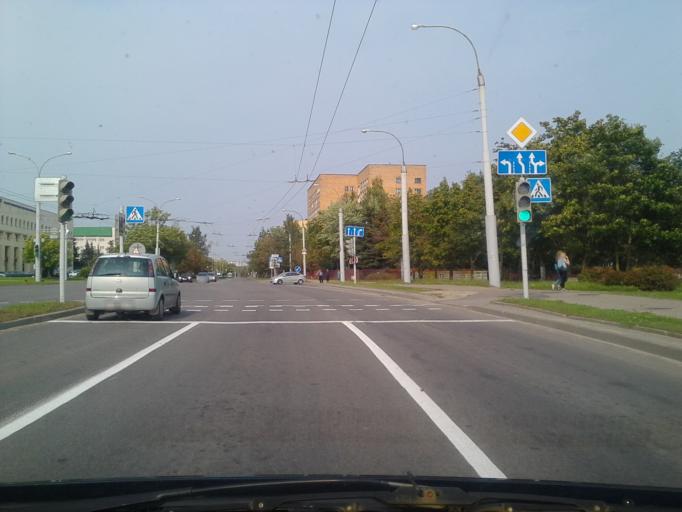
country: BY
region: Minsk
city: Syenitsa
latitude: 53.8573
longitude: 27.4982
